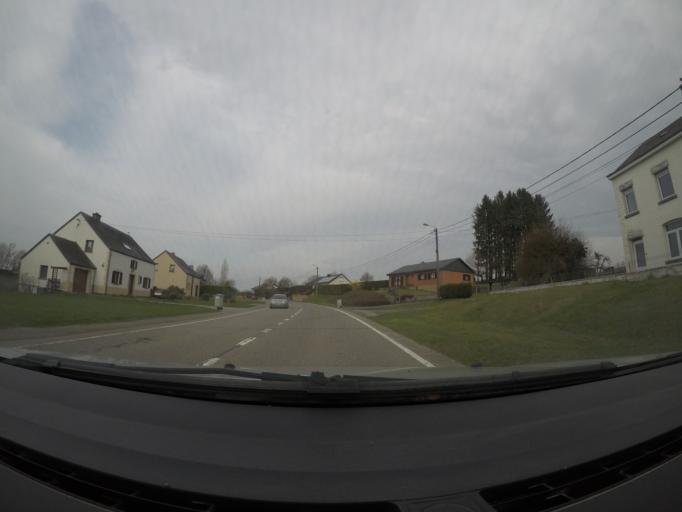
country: BE
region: Wallonia
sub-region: Province du Luxembourg
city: Tintigny
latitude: 49.7174
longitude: 5.5293
